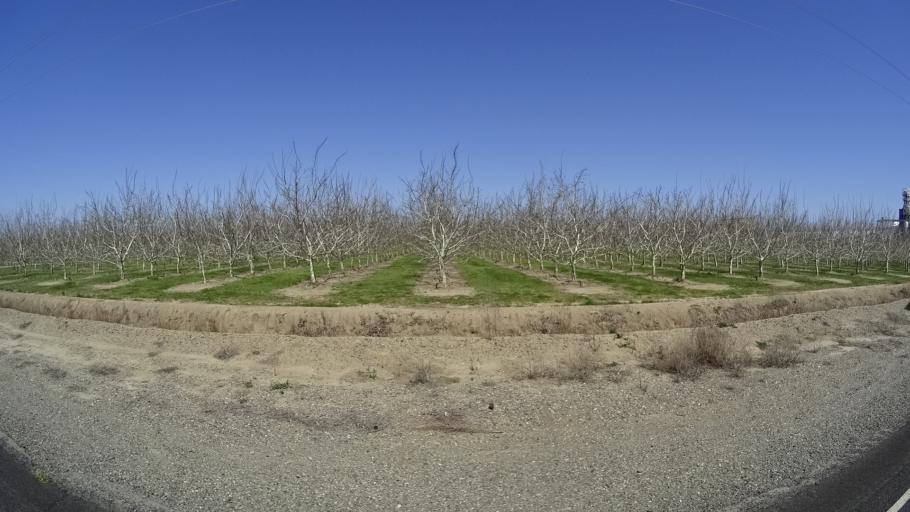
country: US
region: California
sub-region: Glenn County
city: Willows
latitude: 39.4575
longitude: -122.0253
